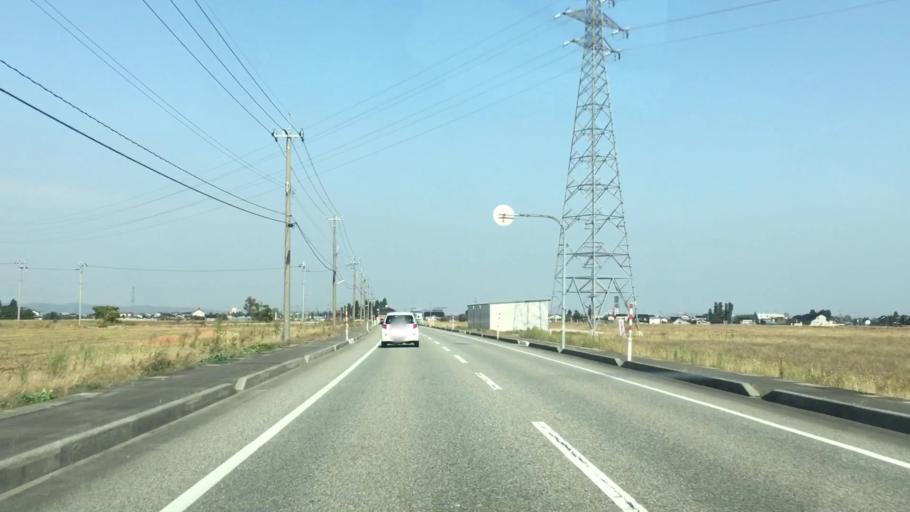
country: JP
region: Toyama
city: Yatsuomachi-higashikumisaka
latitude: 36.6058
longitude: 137.1922
